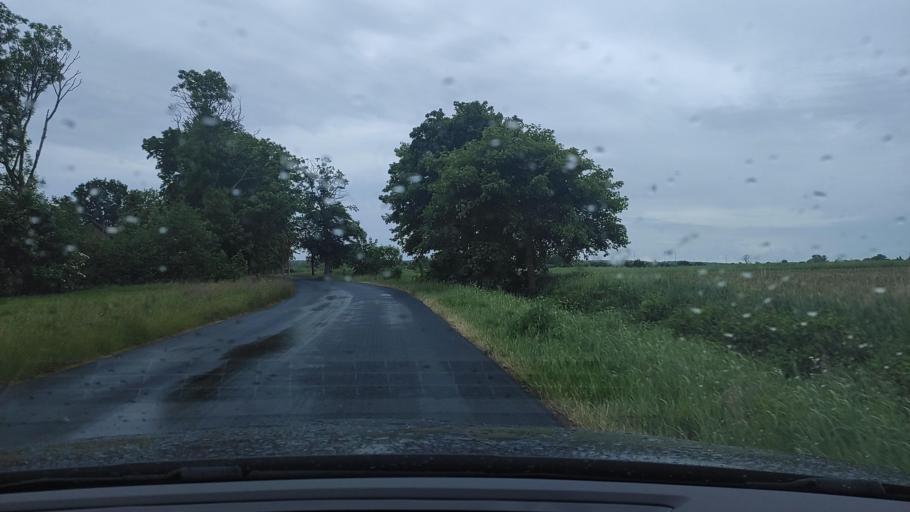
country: PL
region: West Pomeranian Voivodeship
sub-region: Powiat slawienski
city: Slawno
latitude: 54.5139
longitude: 16.5796
